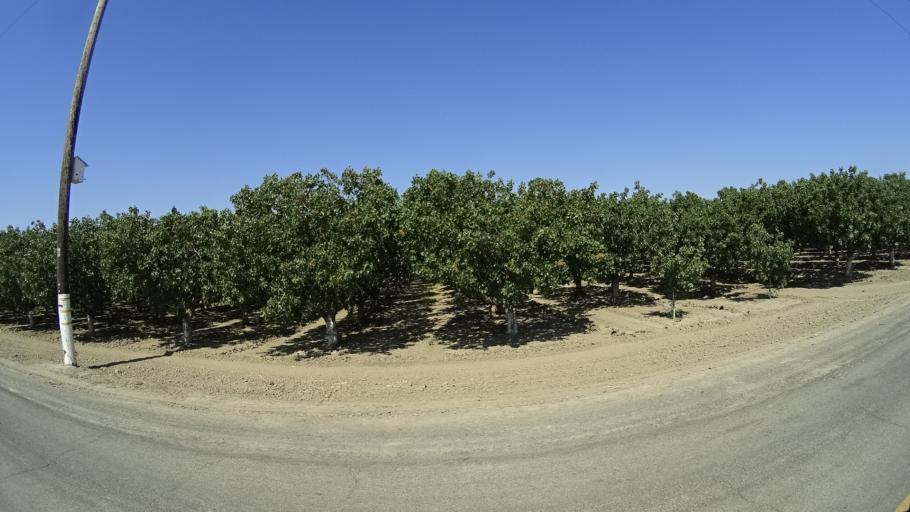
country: US
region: California
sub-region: Kings County
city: Hanford
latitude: 36.3784
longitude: -119.5830
